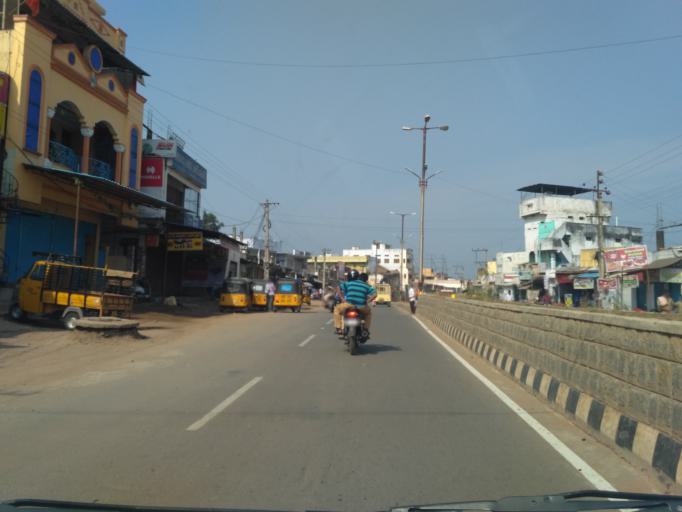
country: IN
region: Telangana
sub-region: Khammam
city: Yellandu
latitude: 17.5857
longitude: 80.3255
